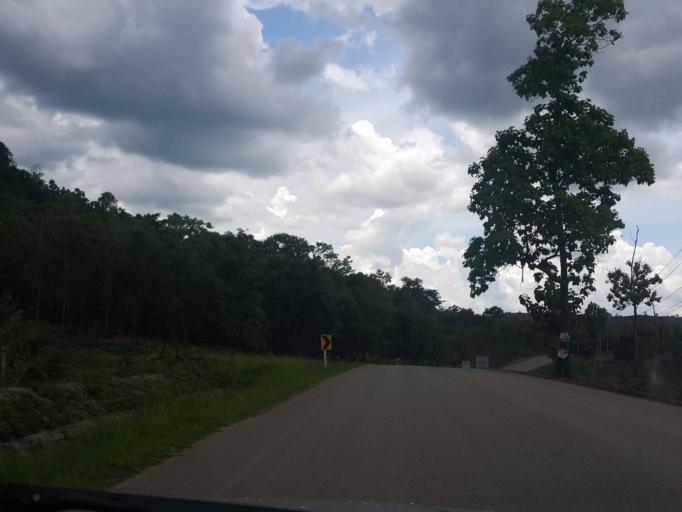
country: TH
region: Phayao
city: Dok Kham Tai
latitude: 18.9730
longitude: 100.0737
